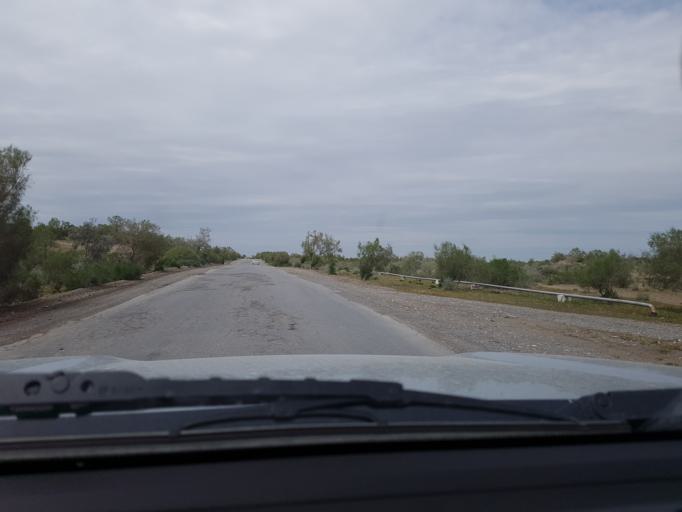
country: TM
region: Lebap
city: Atamyrat
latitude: 38.1132
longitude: 64.7308
